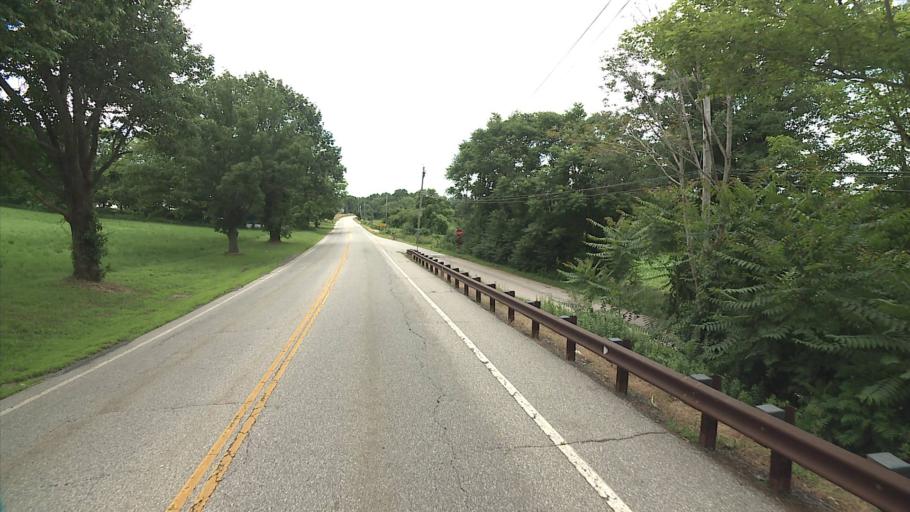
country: US
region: Connecticut
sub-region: New London County
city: Preston City
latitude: 41.5380
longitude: -71.9691
